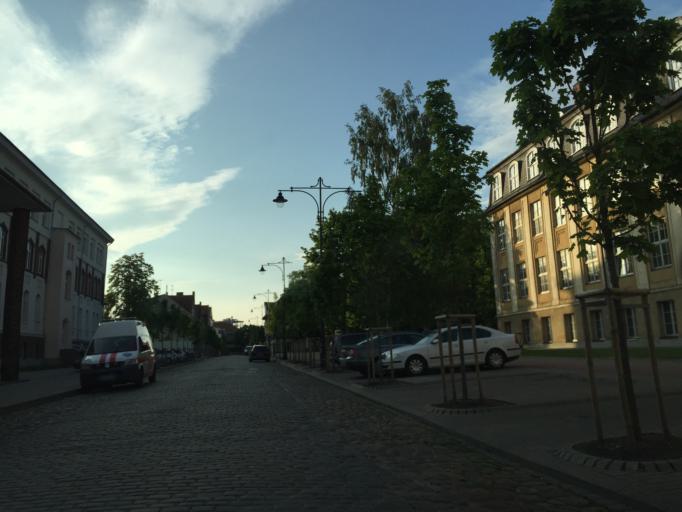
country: LT
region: Klaipedos apskritis
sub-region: Klaipeda
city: Klaipeda
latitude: 55.7146
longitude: 21.1365
